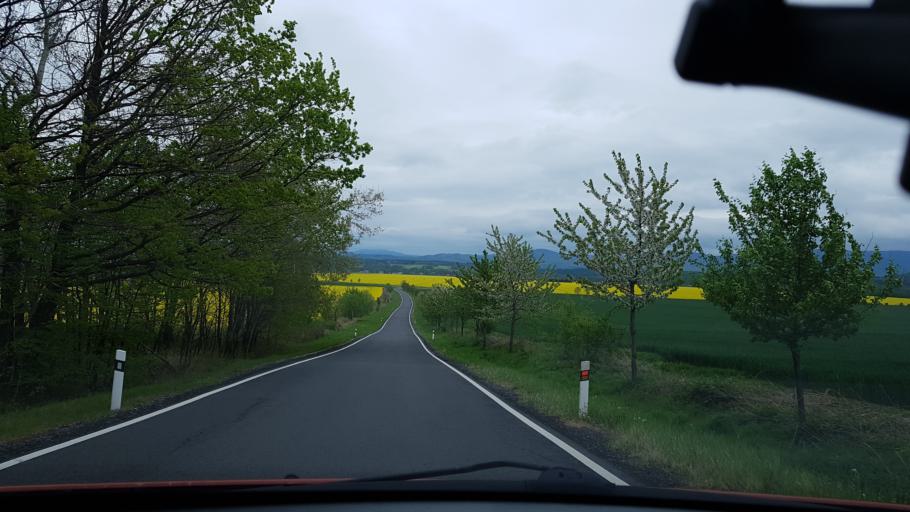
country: CZ
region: Olomoucky
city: Vidnava
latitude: 50.3852
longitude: 17.1365
